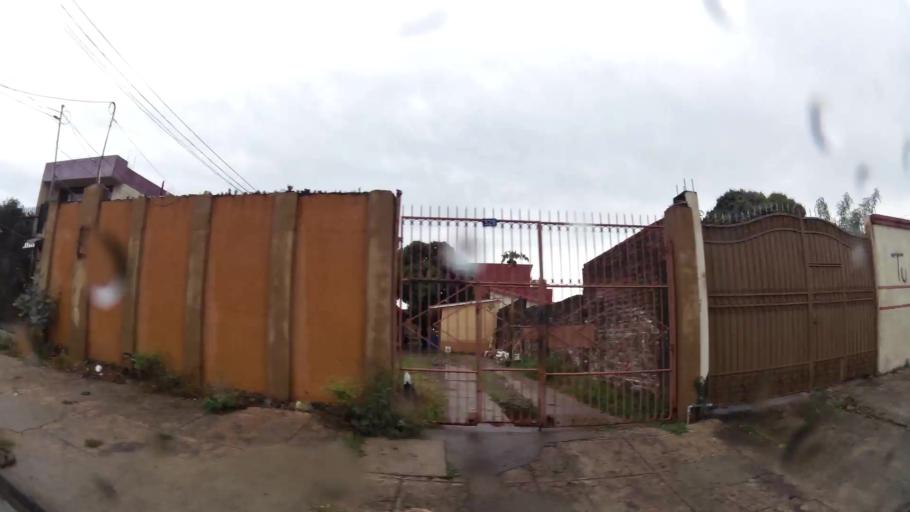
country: BO
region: Santa Cruz
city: Santa Cruz de la Sierra
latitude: -17.8072
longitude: -63.1914
